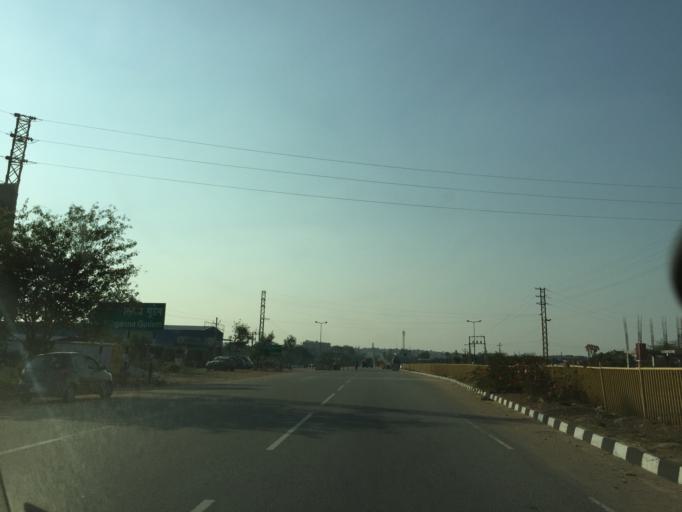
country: IN
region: Telangana
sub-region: Nalgonda
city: Bhongir
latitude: 17.5009
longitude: 78.8833
